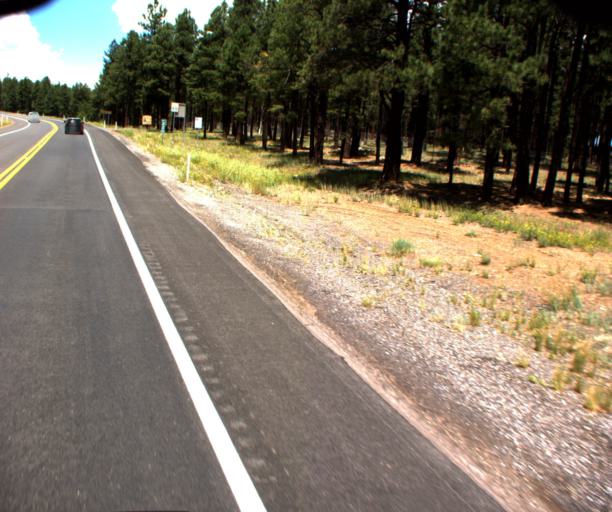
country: US
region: Arizona
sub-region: Coconino County
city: Flagstaff
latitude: 35.2452
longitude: -111.6862
